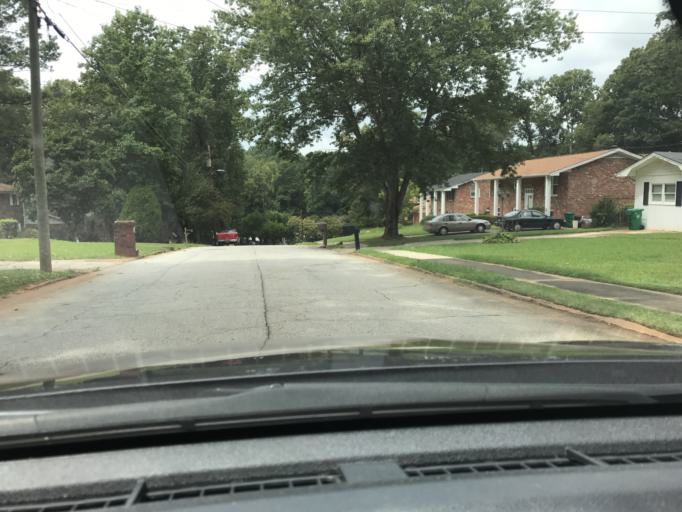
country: US
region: Georgia
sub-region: DeKalb County
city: Belvedere Park
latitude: 33.7462
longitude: -84.2414
